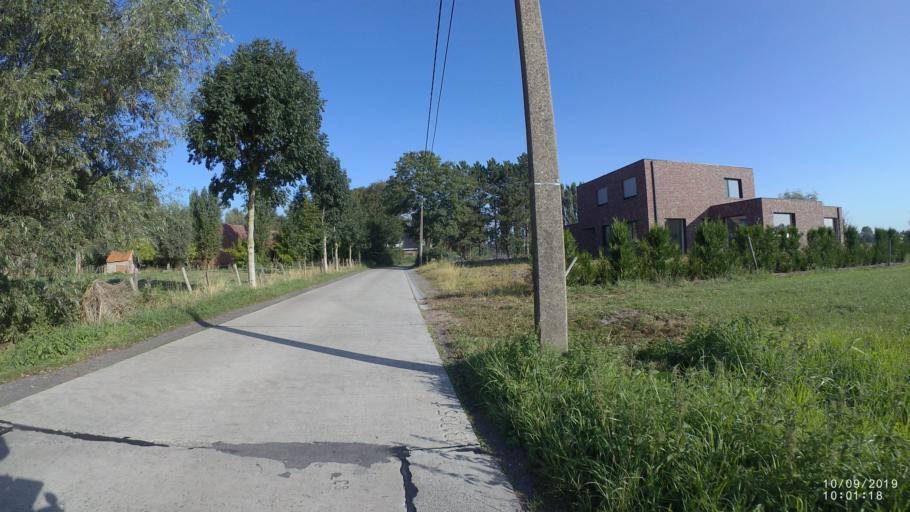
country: BE
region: Flanders
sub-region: Provincie Oost-Vlaanderen
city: Lochristi
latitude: 51.1251
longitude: 3.8281
